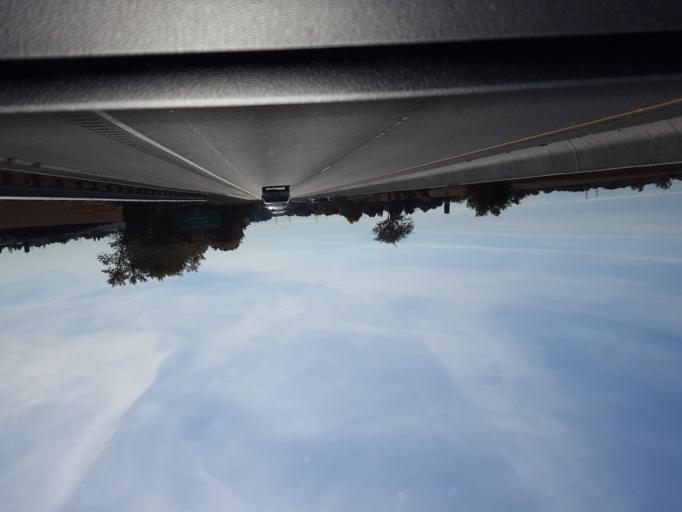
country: CA
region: Ontario
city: Oshawa
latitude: 43.9211
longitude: -78.6061
